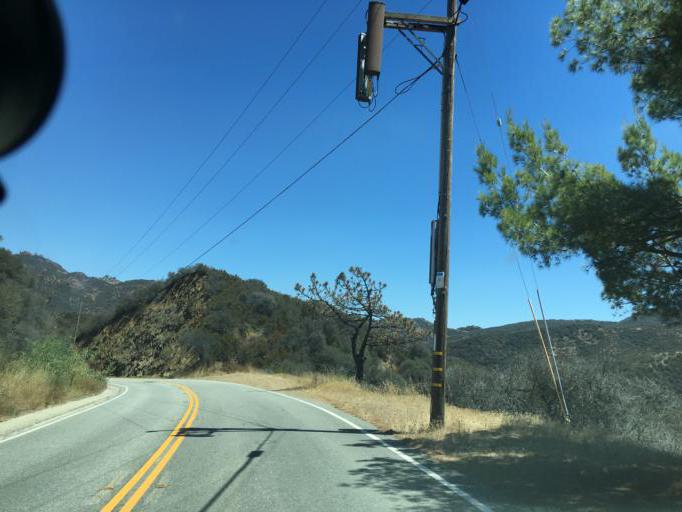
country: US
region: California
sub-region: Los Angeles County
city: Westlake Village
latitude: 34.0852
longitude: -118.8609
